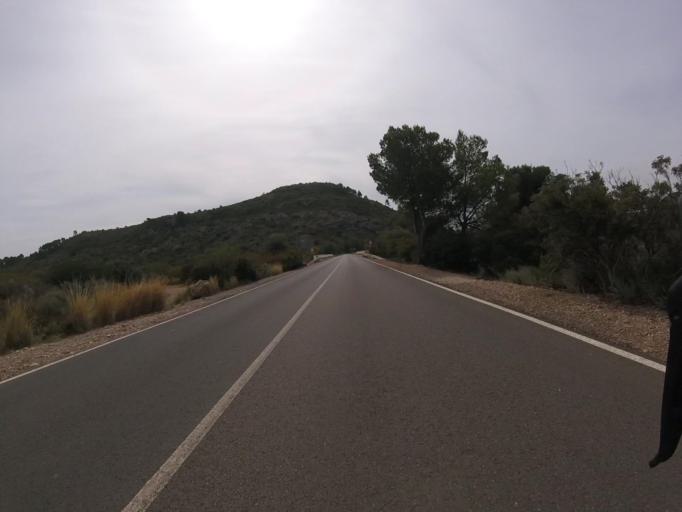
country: ES
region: Valencia
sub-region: Provincia de Castello
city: Benicassim
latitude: 40.0607
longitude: 0.0449
